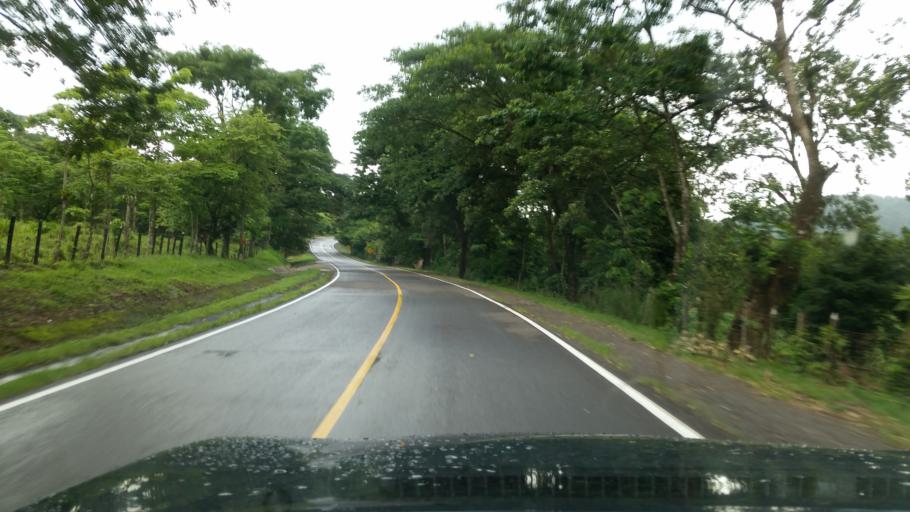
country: NI
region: Matagalpa
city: San Ramon
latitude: 13.0500
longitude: -85.7629
